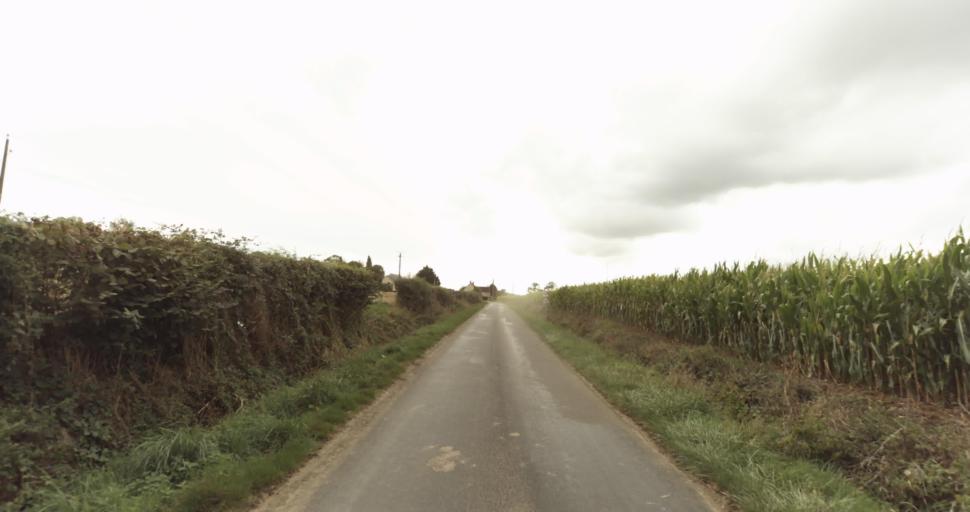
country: FR
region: Lower Normandy
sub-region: Departement de l'Orne
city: Gace
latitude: 48.6945
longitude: 0.2530
